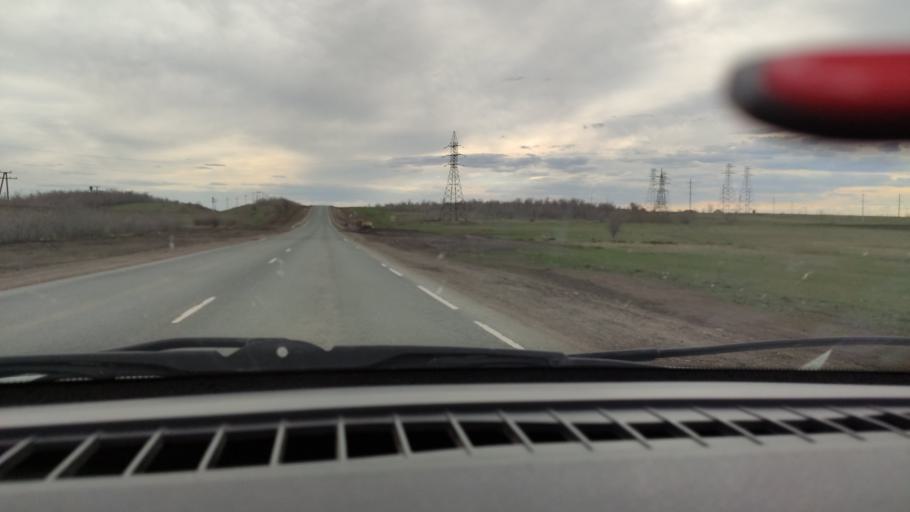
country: RU
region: Bashkortostan
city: Mayachnyy
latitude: 52.3436
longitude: 55.5398
